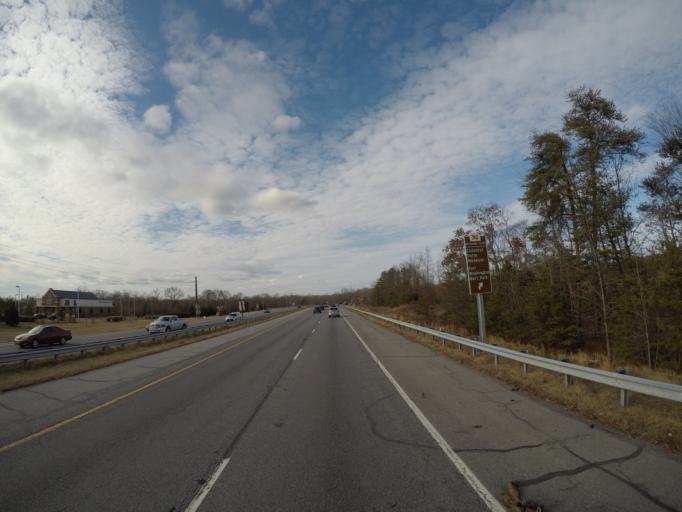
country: US
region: Maryland
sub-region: Prince George's County
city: Accokeek
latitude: 38.6617
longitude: -77.0153
